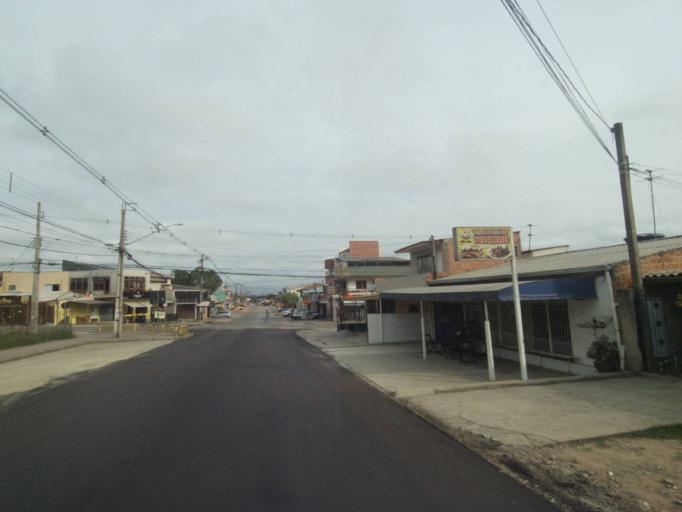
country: BR
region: Parana
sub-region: Sao Jose Dos Pinhais
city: Sao Jose dos Pinhais
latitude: -25.5494
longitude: -49.2717
